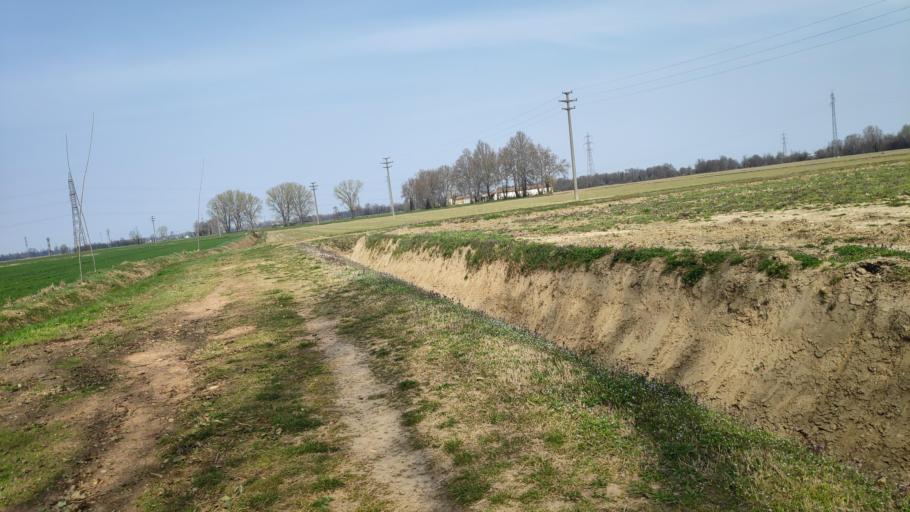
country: IT
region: Lombardy
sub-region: Citta metropolitana di Milano
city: Pantigliate
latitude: 45.4436
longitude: 9.3648
